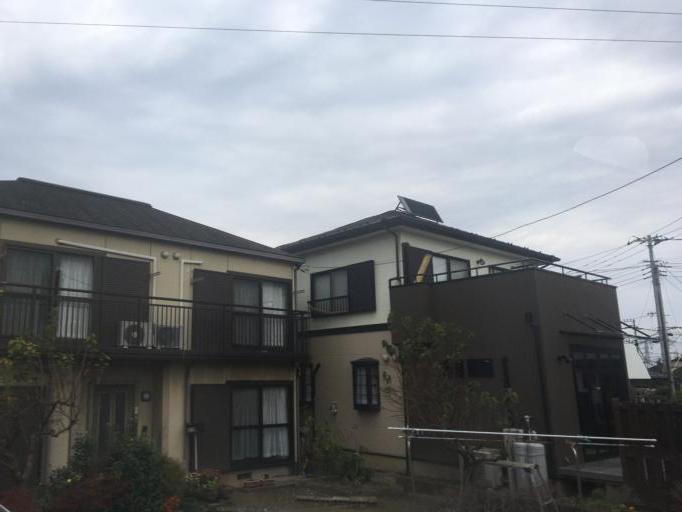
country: JP
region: Saitama
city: Hanno
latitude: 35.8447
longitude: 139.3317
